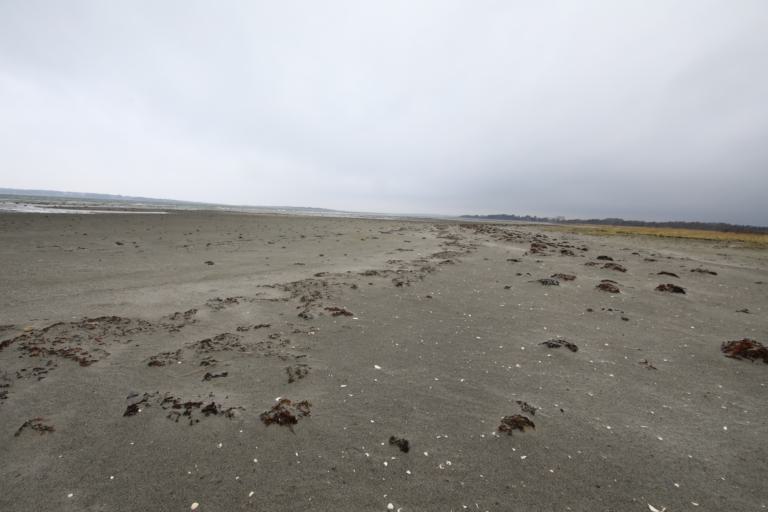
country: SE
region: Halland
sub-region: Kungsbacka Kommun
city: Frillesas
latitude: 57.3034
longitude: 12.1653
